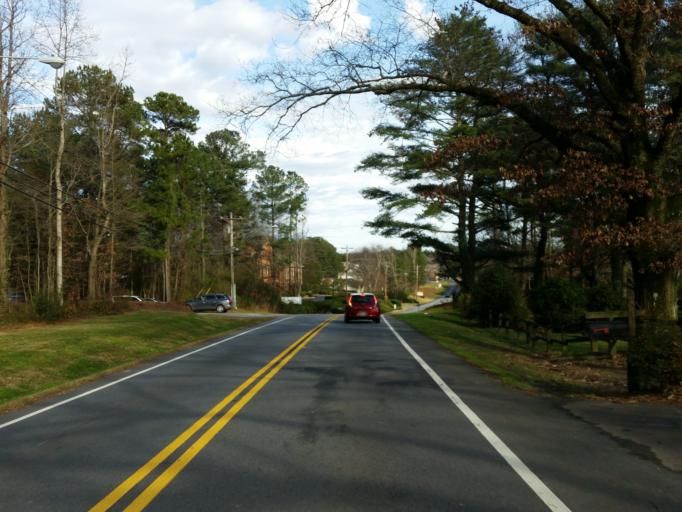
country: US
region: Georgia
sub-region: Fulton County
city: Sandy Springs
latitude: 33.9488
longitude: -84.4163
